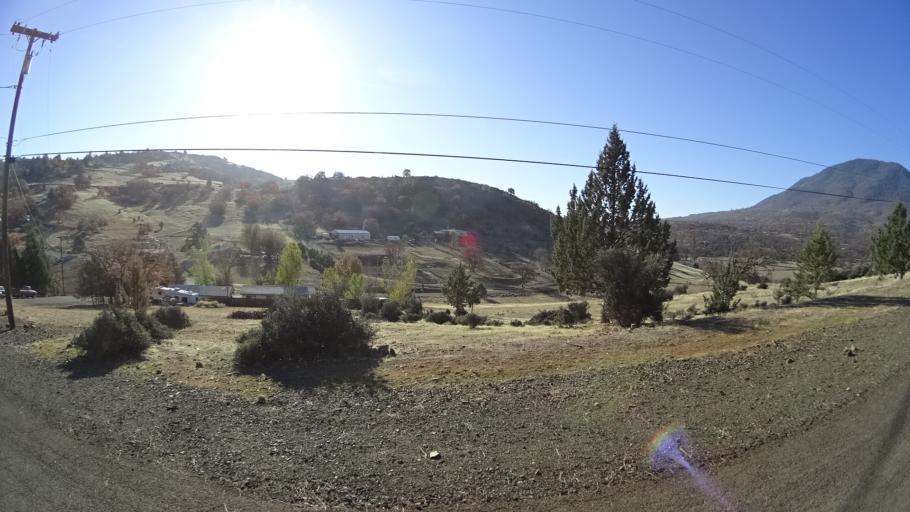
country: US
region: California
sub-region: Siskiyou County
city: Montague
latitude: 41.8951
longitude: -122.4802
